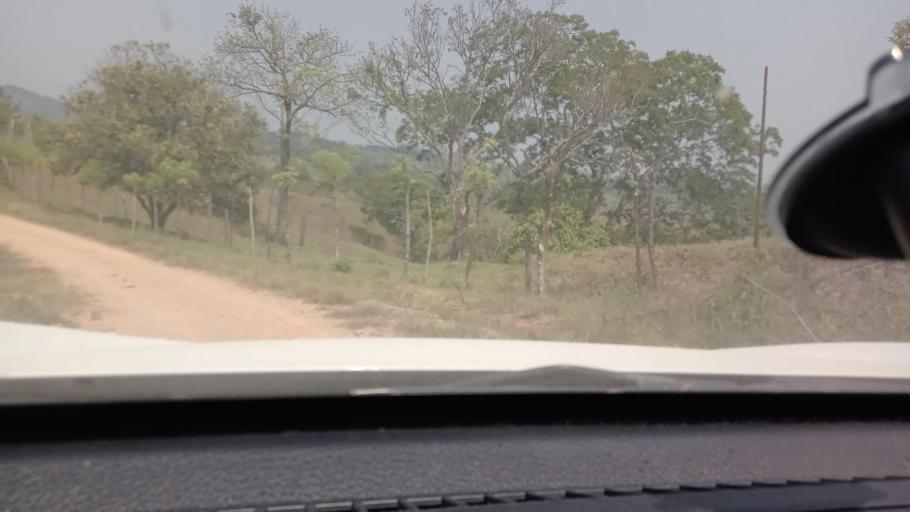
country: MX
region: Tabasco
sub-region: Huimanguillo
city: Francisco Rueda
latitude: 17.4949
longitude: -93.9263
